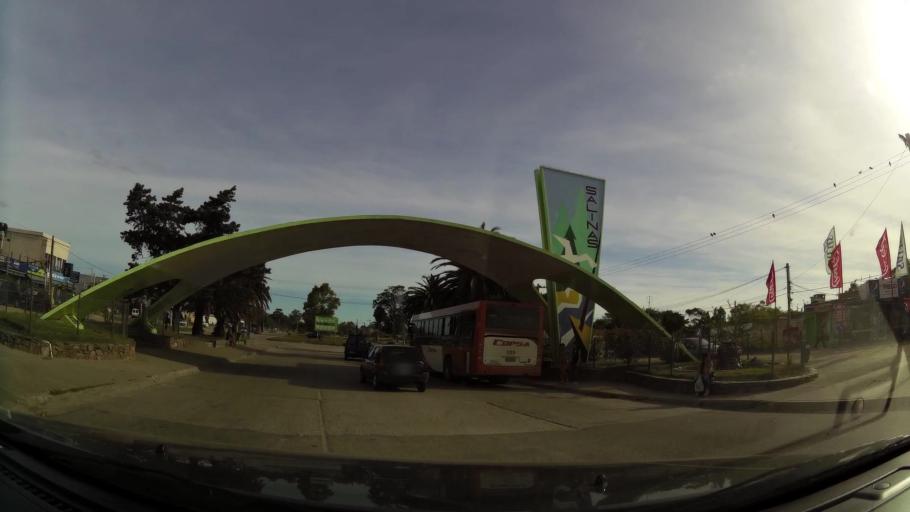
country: UY
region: Canelones
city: Atlantida
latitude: -34.7755
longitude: -55.8400
